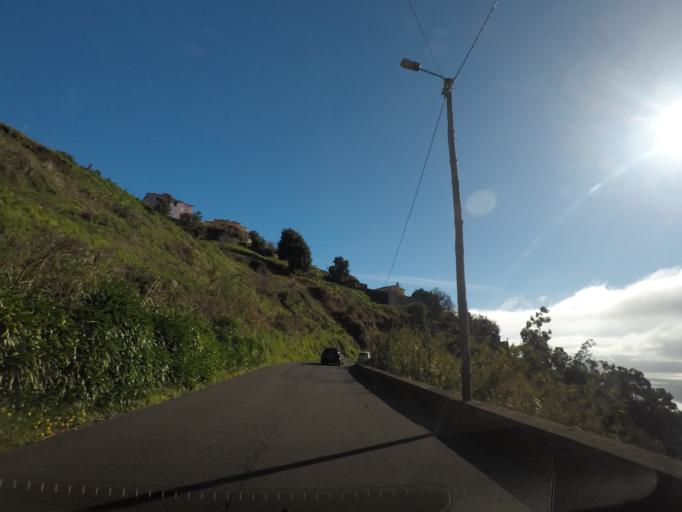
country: PT
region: Madeira
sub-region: Calheta
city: Arco da Calheta
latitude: 32.7306
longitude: -17.1526
